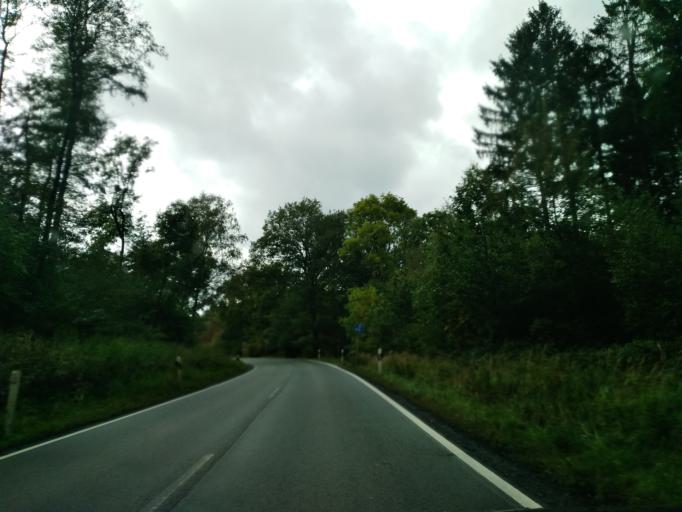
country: DE
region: Rheinland-Pfalz
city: Windhagen
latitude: 50.6556
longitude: 7.3420
